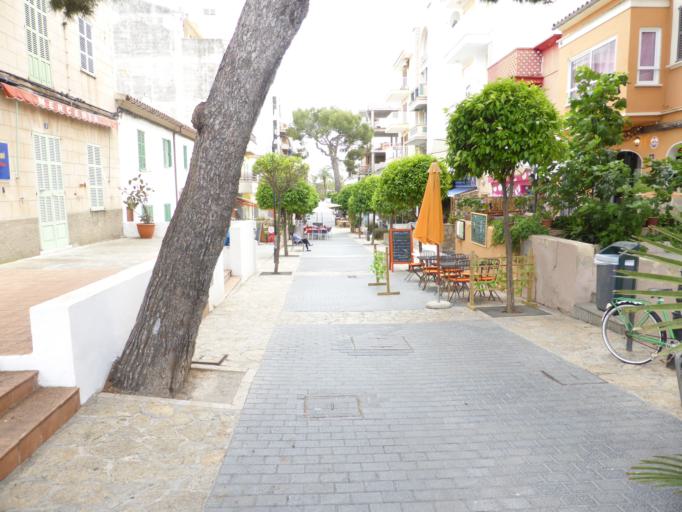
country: ES
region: Balearic Islands
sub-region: Illes Balears
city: Port d'Alcudia
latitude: 39.8425
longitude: 3.1347
